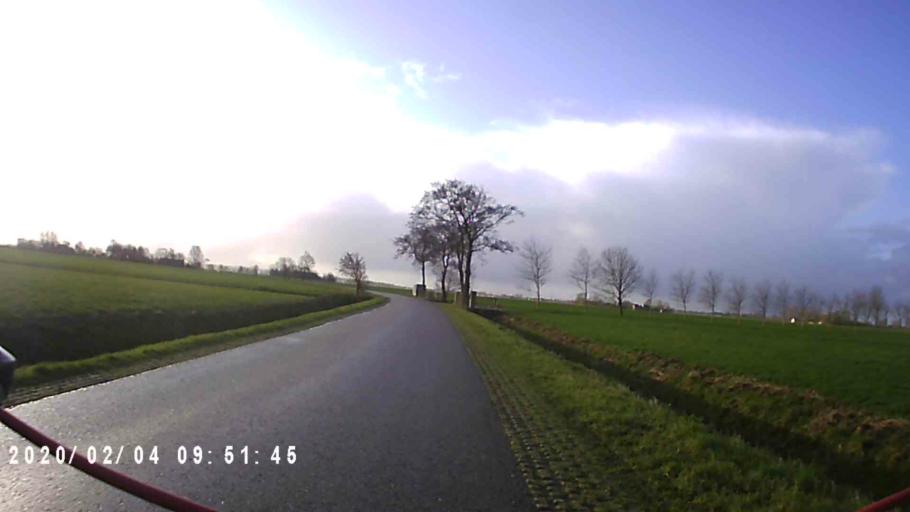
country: NL
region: Groningen
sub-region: Gemeente Zuidhorn
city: Aduard
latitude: 53.2864
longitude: 6.4943
